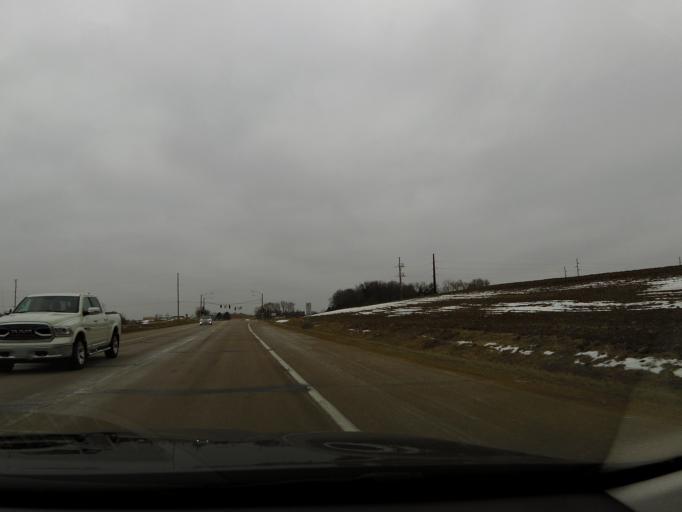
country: US
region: Minnesota
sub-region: Carver County
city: Carver
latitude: 44.8074
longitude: -93.6493
